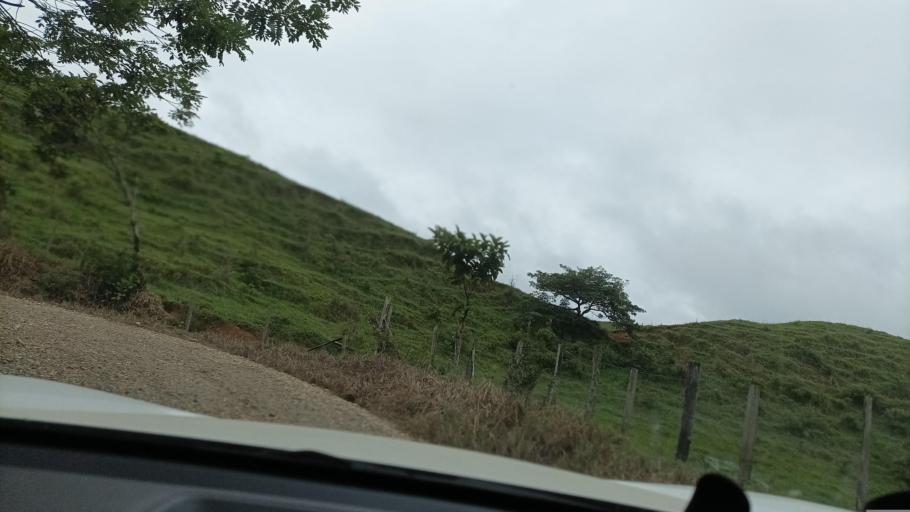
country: MX
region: Veracruz
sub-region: Uxpanapa
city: Poblado 10
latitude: 17.4390
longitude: -94.4150
